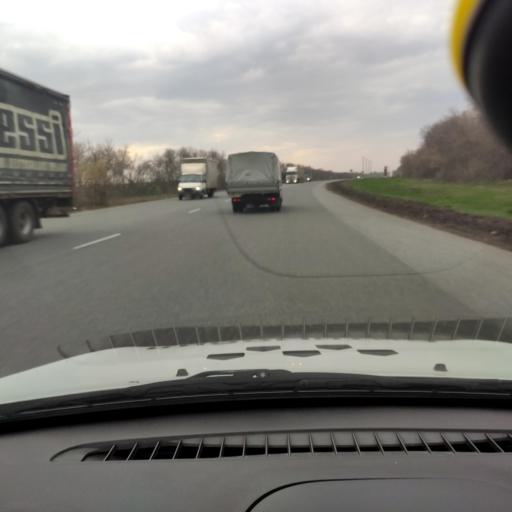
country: RU
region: Samara
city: Mezhdurechensk
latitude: 53.2655
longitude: 49.2776
